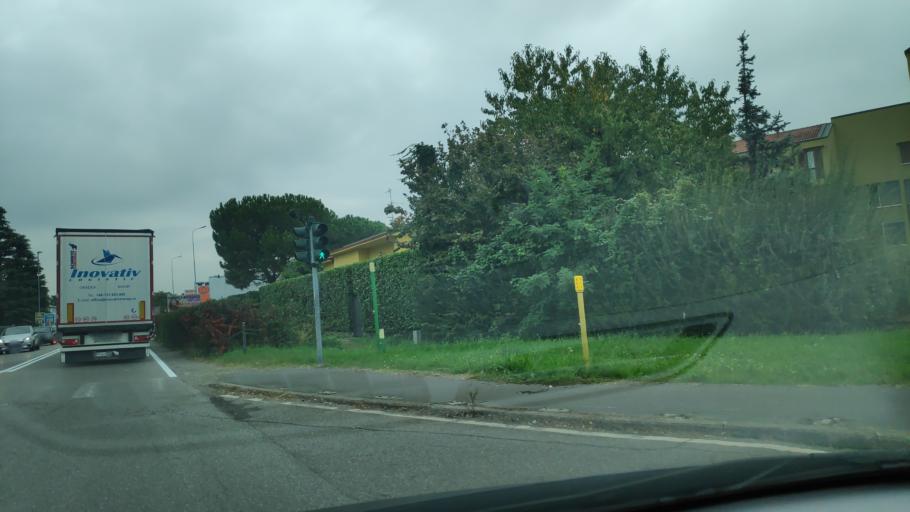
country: IT
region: Lombardy
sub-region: Citta metropolitana di Milano
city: Legnano
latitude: 45.6087
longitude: 8.9196
